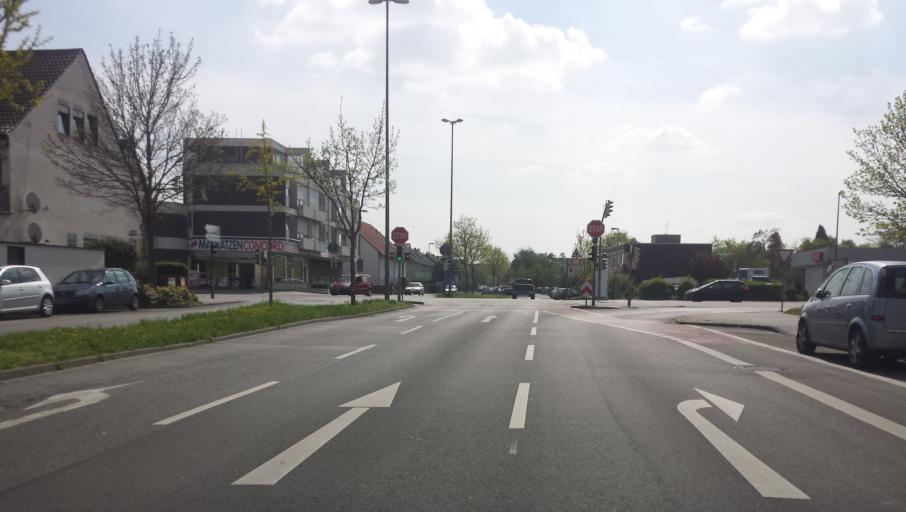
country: DE
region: Rheinland-Pfalz
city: Gartenstadt
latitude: 49.4585
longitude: 8.4030
